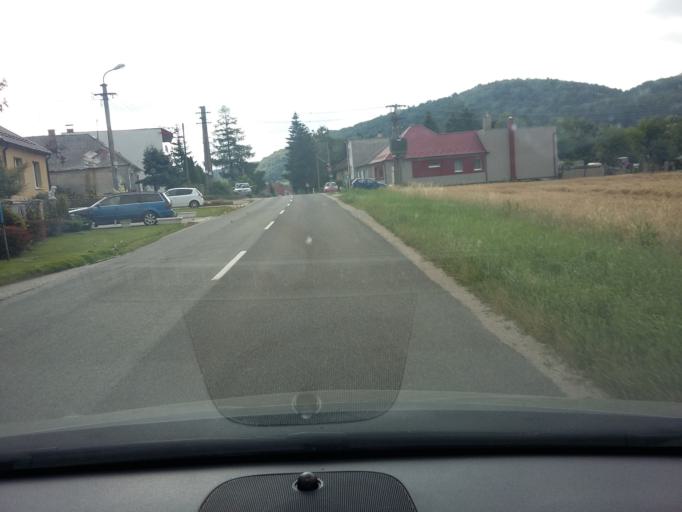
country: SK
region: Trnavsky
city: Smolenice
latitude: 48.5428
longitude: 17.3887
